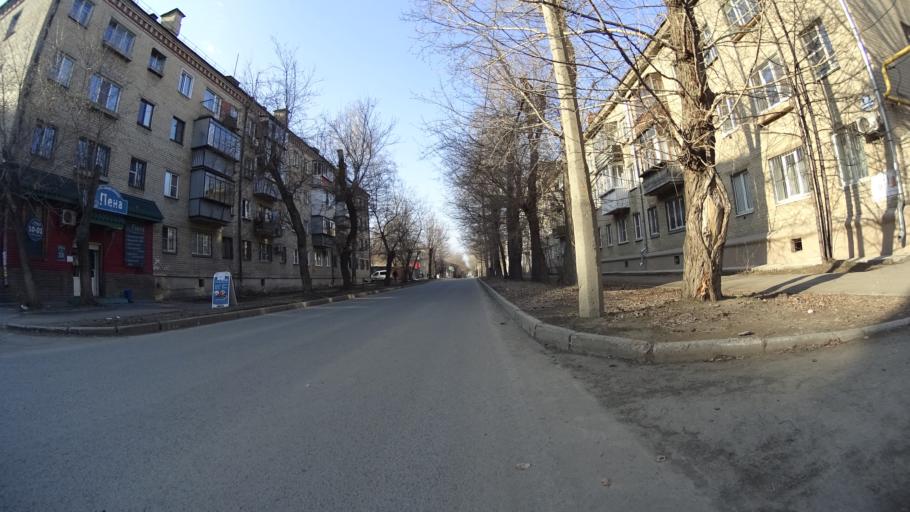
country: RU
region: Chelyabinsk
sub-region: Gorod Chelyabinsk
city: Chelyabinsk
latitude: 55.1445
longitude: 61.3750
